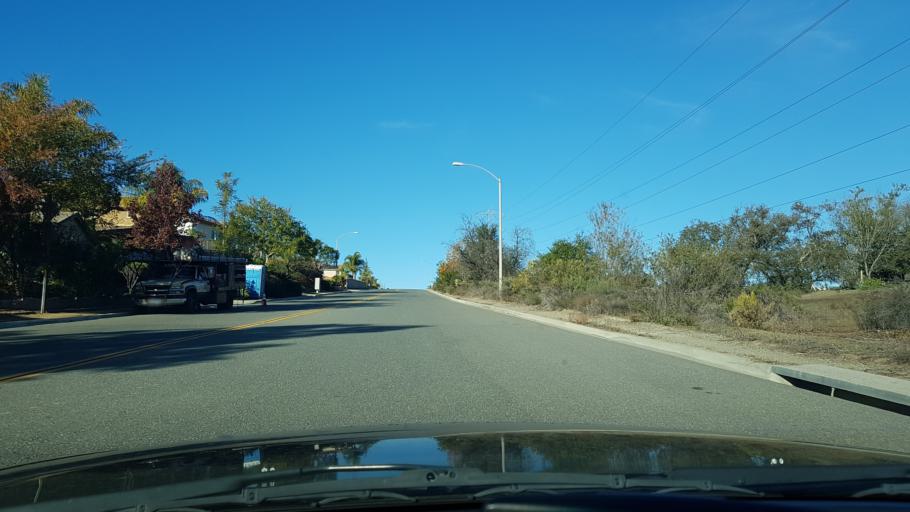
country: US
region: California
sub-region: San Diego County
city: Hidden Meadows
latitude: 33.2157
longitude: -117.0954
